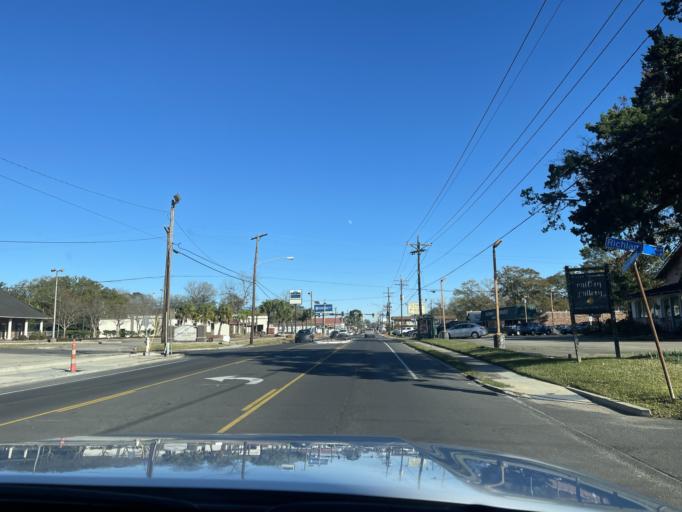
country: US
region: Louisiana
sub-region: East Baton Rouge Parish
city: Baton Rouge
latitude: 30.4443
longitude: -91.1488
